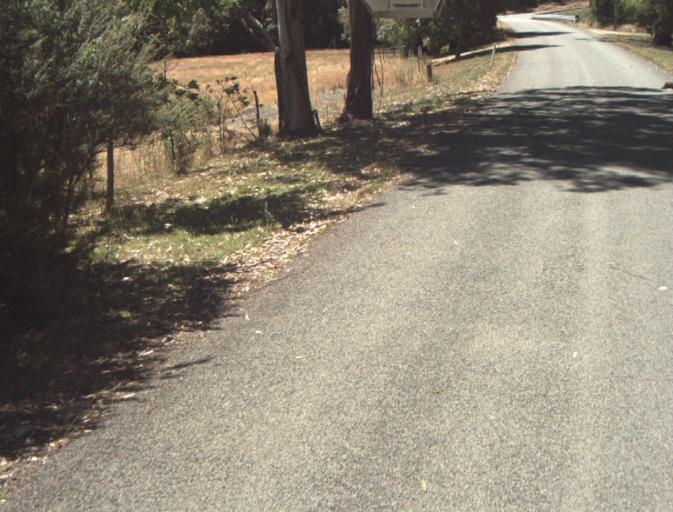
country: AU
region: Tasmania
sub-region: Dorset
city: Scottsdale
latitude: -41.2941
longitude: 147.4065
